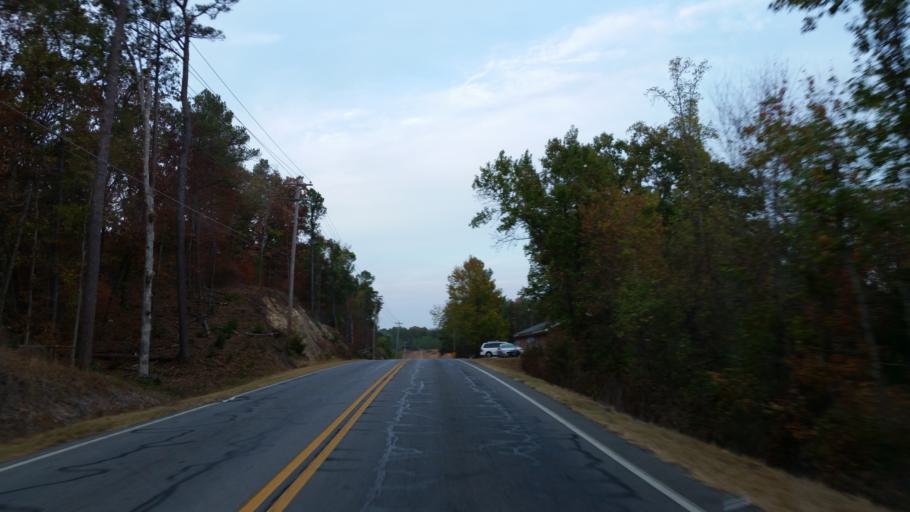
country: US
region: Georgia
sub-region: Gordon County
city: Calhoun
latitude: 34.5902
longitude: -84.9346
